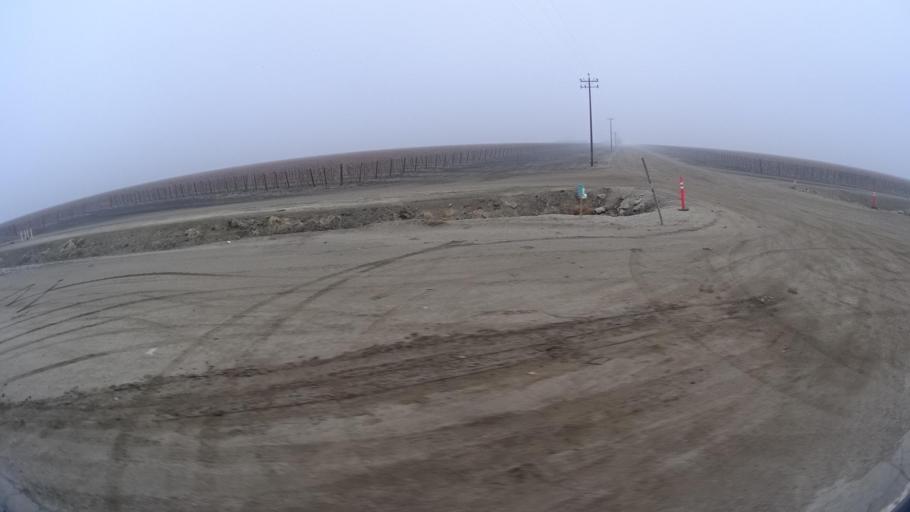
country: US
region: California
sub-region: Kern County
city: Lost Hills
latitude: 35.5139
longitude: -119.6153
